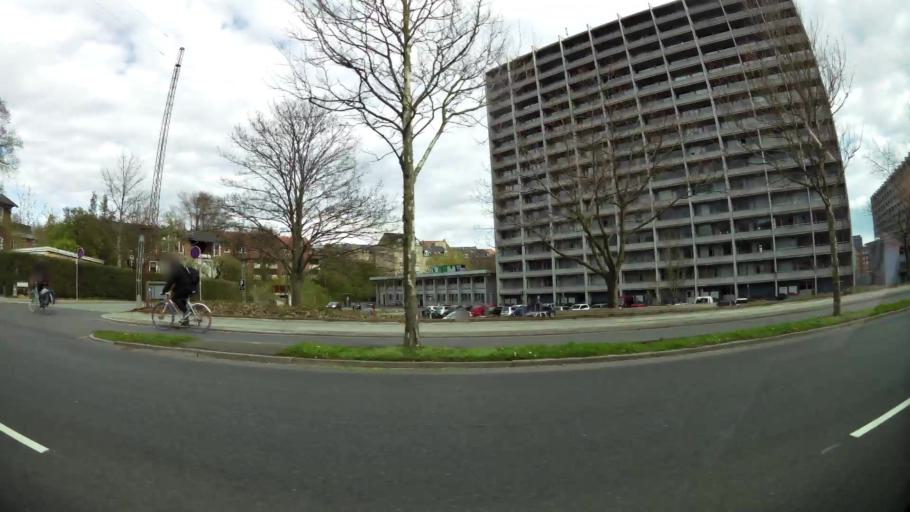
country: DK
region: Central Jutland
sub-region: Arhus Kommune
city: Arhus
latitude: 56.1635
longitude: 10.1970
